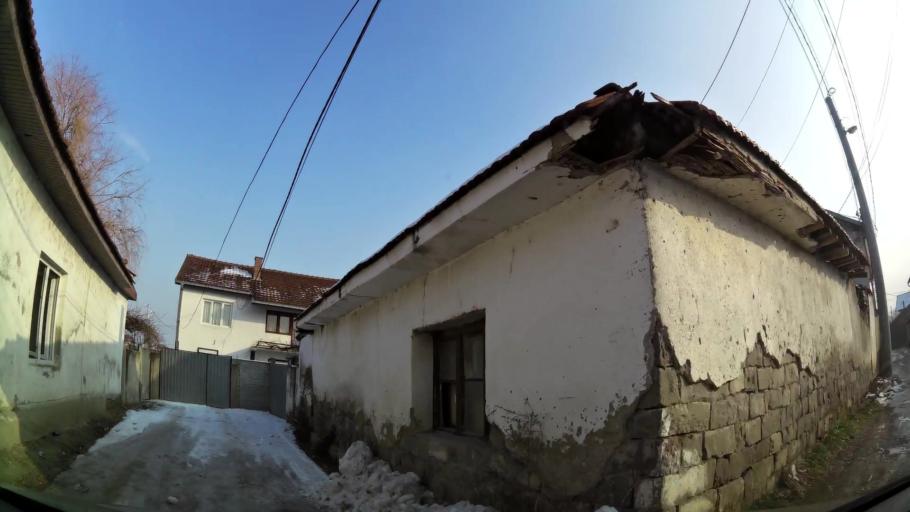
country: MK
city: Creshevo
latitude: 42.0216
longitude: 21.5072
